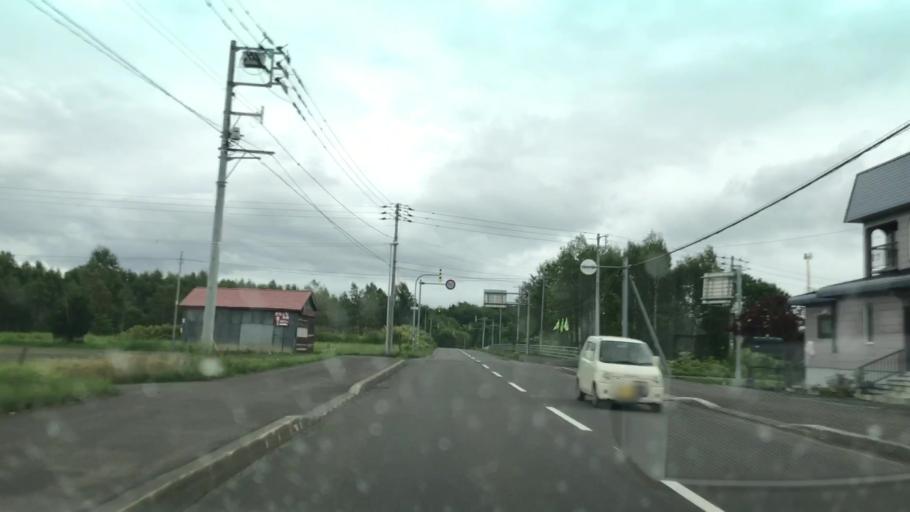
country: JP
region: Hokkaido
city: Niseko Town
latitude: 42.7960
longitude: 140.7125
